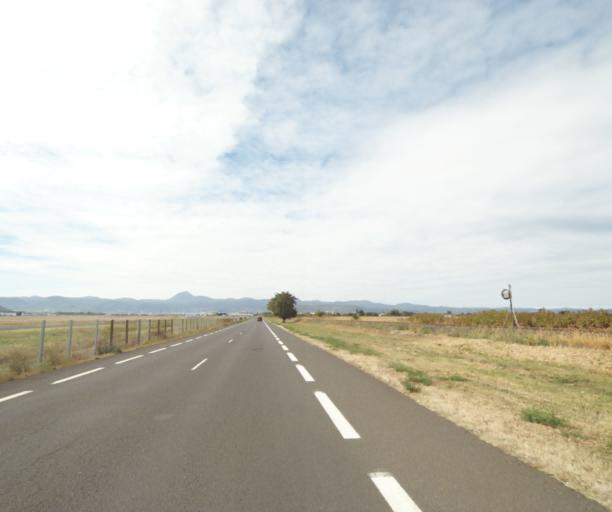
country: FR
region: Auvergne
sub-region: Departement du Puy-de-Dome
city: Aulnat
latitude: 45.7909
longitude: 3.1837
